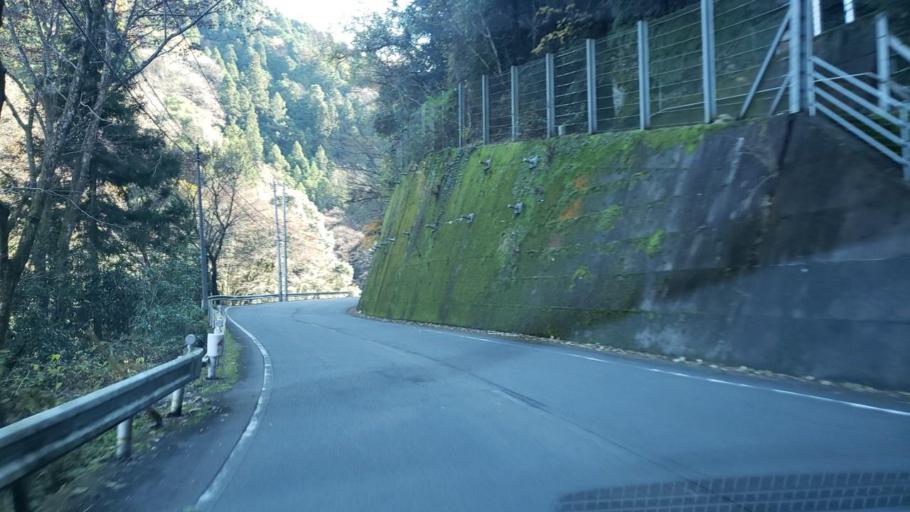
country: JP
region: Tokushima
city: Wakimachi
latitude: 34.0131
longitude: 134.0313
